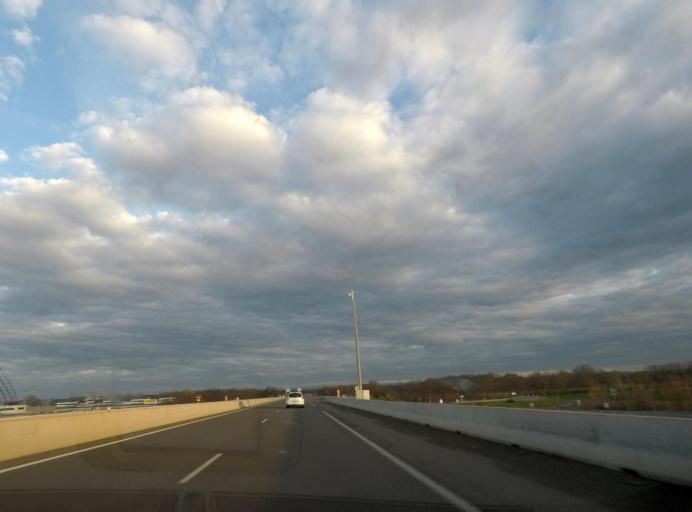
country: FR
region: Bourgogne
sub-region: Departement de Saone-et-Loire
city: Charnay-les-Macon
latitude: 46.2771
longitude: 4.8048
